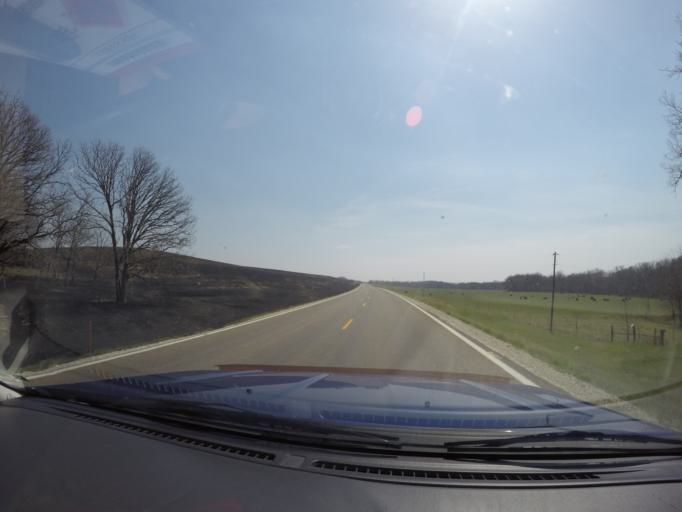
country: US
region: Kansas
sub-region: Chase County
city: Cottonwood Falls
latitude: 38.4786
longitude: -96.5572
